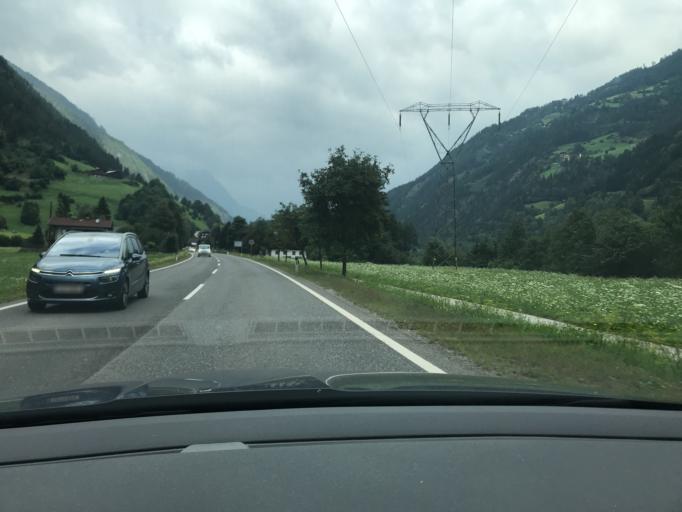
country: AT
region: Tyrol
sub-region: Politischer Bezirk Lienz
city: Hopfgarten in Defereggen
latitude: 46.9437
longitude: 12.5679
